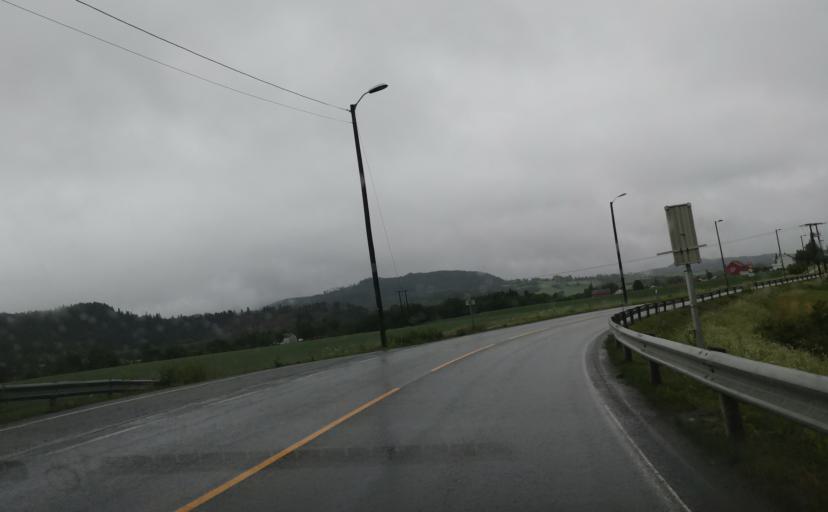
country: NO
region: Nord-Trondelag
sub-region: Stjordal
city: Stjordalshalsen
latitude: 63.4436
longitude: 10.9232
